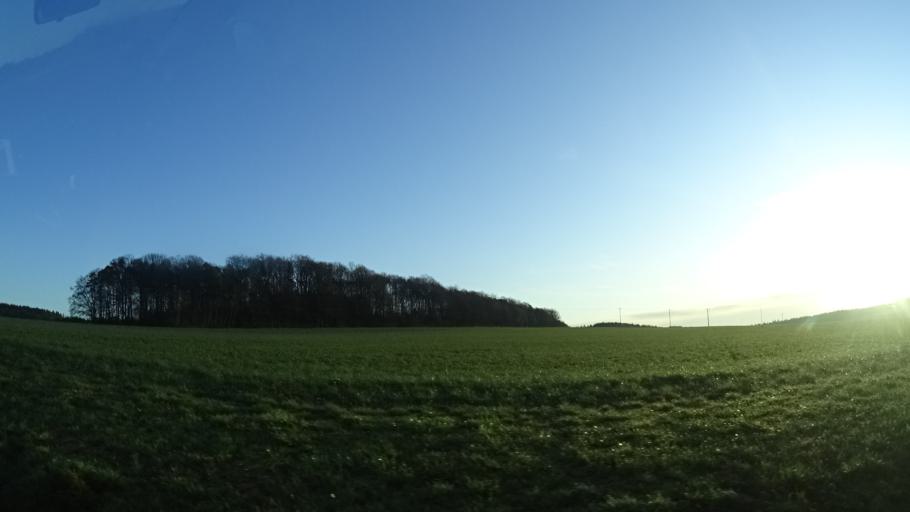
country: DE
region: Bavaria
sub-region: Regierungsbezirk Unterfranken
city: Miltenberg
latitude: 49.6650
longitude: 9.2814
